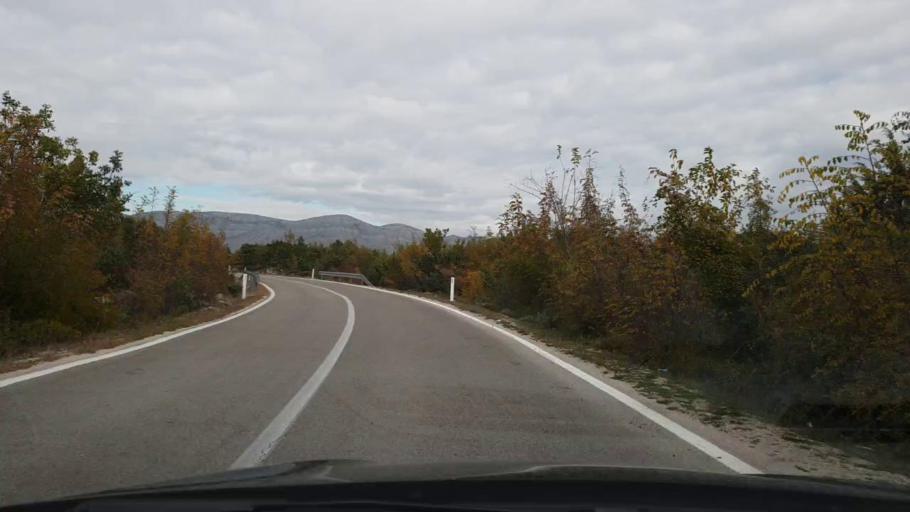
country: HR
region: Dubrovacko-Neretvanska
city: Cibaca
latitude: 42.6754
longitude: 18.2351
